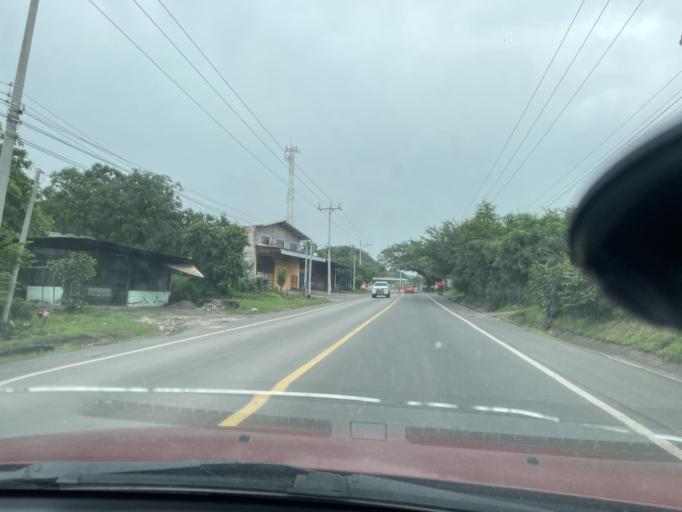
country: SV
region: San Miguel
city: San Miguel
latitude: 13.5157
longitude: -88.1450
